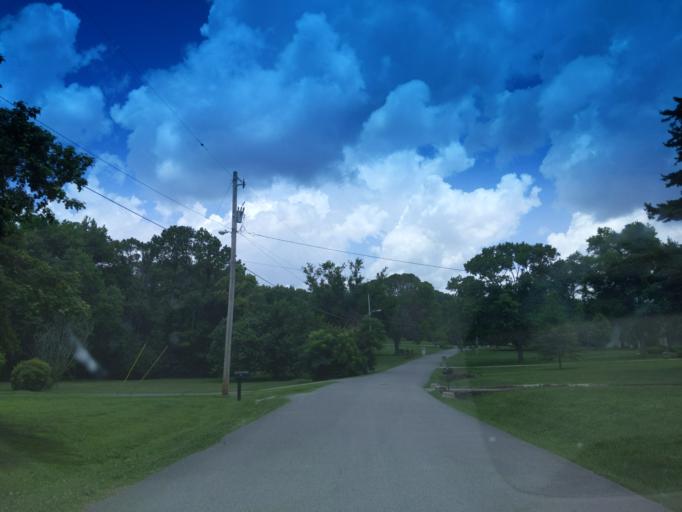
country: US
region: Tennessee
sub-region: Williamson County
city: Brentwood Estates
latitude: 36.0251
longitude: -86.7752
